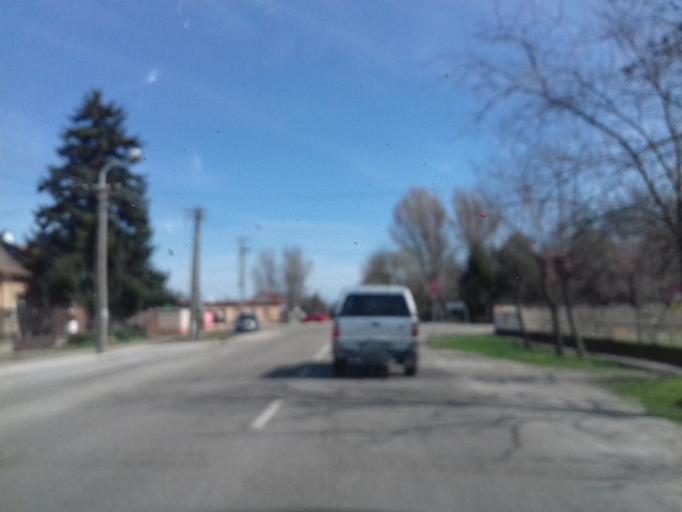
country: HU
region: Bacs-Kiskun
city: Kecskemet
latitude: 46.8954
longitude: 19.7260
